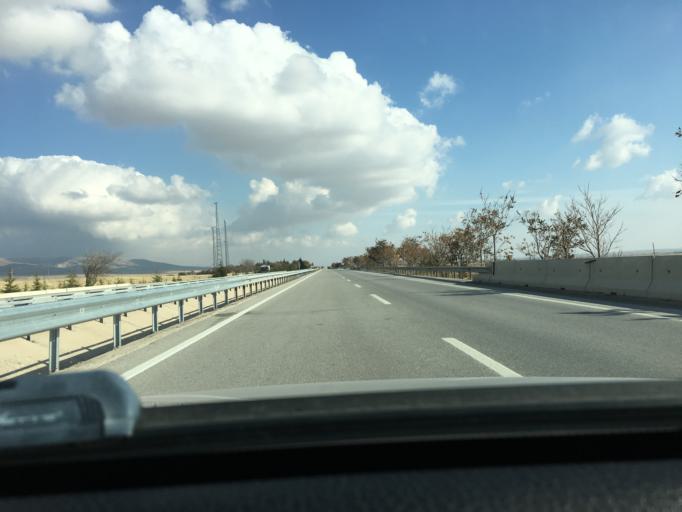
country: TR
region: Eskisehir
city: Kaymaz
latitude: 39.4775
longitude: 31.3149
